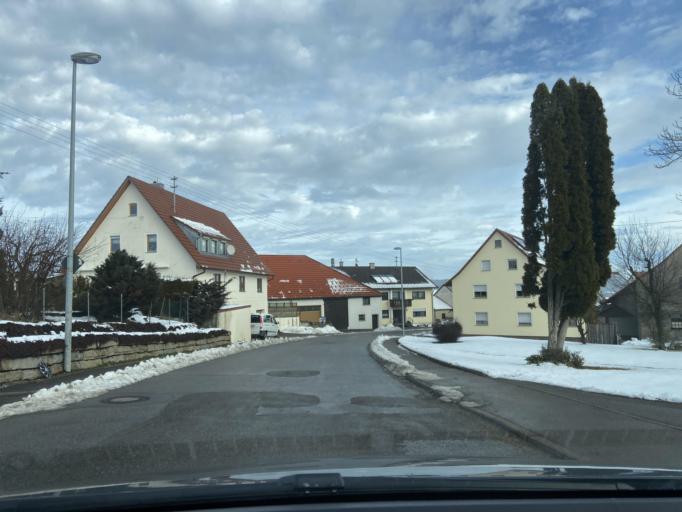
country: DE
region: Baden-Wuerttemberg
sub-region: Tuebingen Region
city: Gammertingen
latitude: 48.2541
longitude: 9.2680
